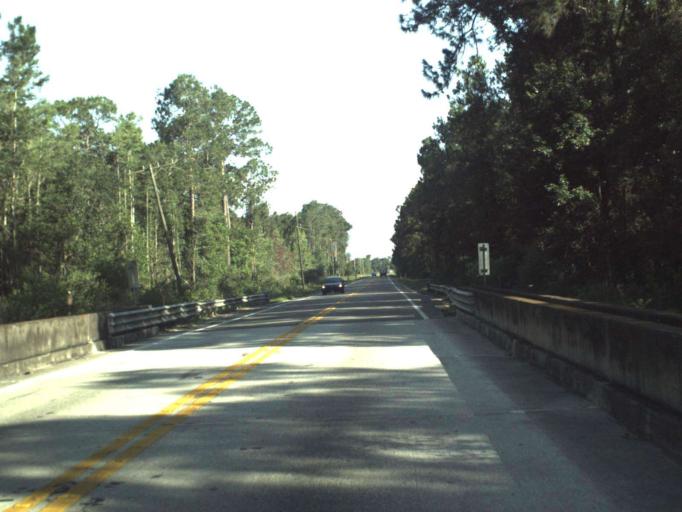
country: US
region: Florida
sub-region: Lake County
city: Clermont
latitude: 28.3975
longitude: -81.8272
